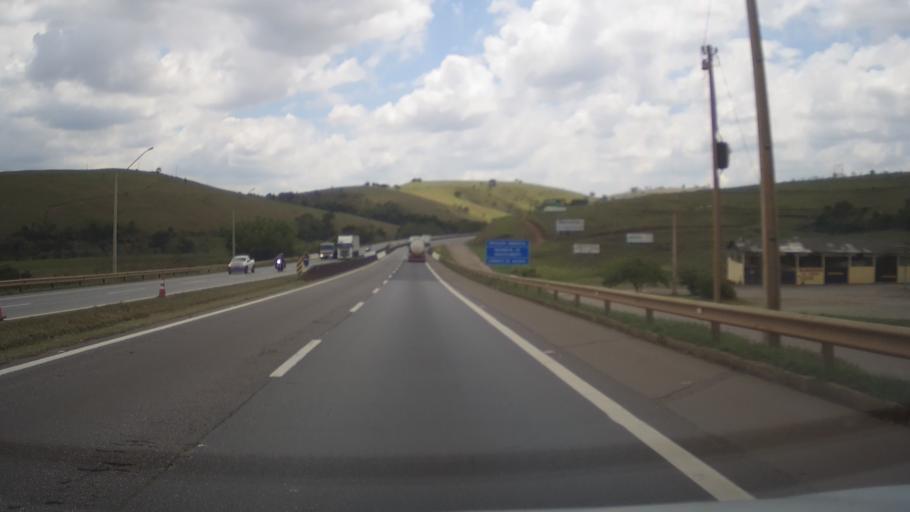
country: BR
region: Minas Gerais
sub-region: Tres Coracoes
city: Tres Coracoes
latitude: -21.7125
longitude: -45.3759
